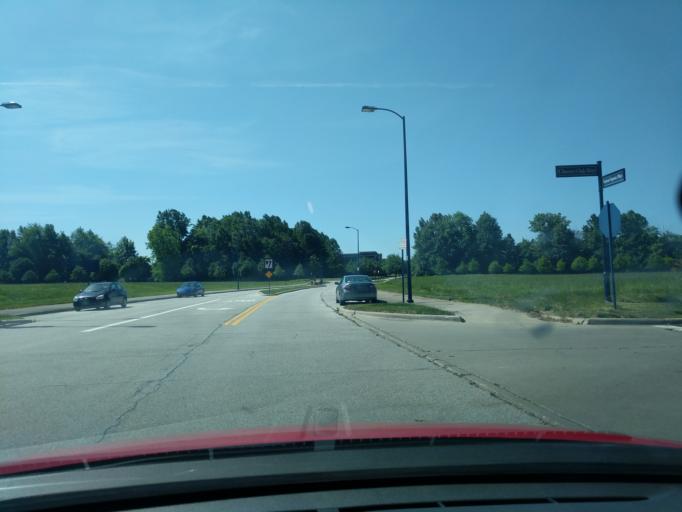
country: US
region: Ohio
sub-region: Franklin County
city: Minerva Park
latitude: 40.0466
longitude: -82.9153
